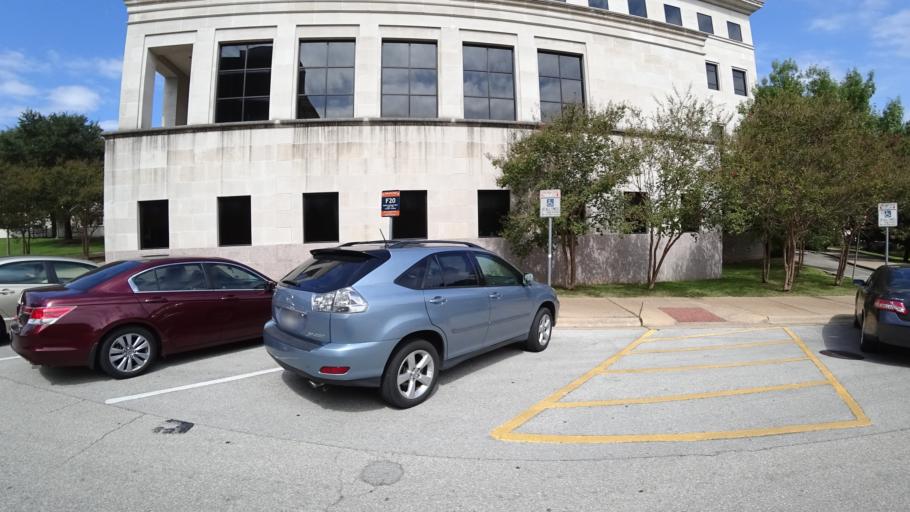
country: US
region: Texas
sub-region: Travis County
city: Austin
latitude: 30.2878
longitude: -97.7306
